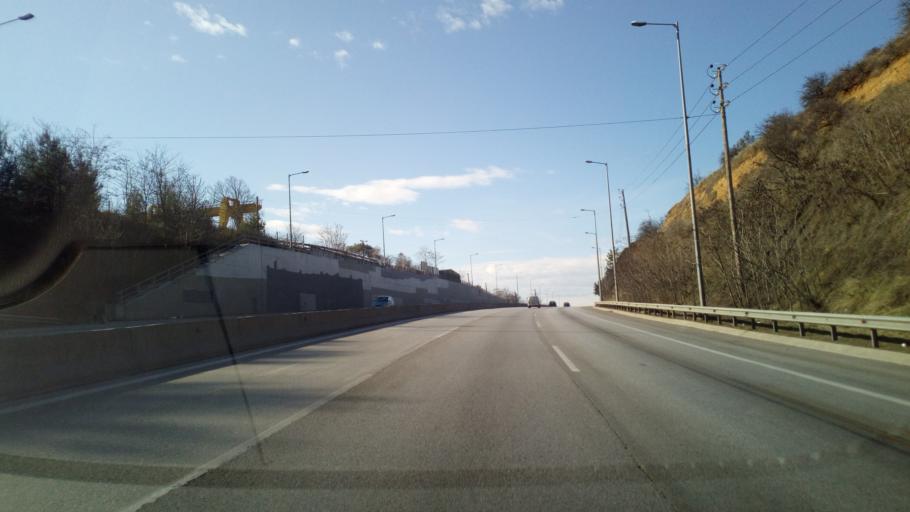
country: GR
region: Central Macedonia
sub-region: Nomos Thessalonikis
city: Liti
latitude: 40.7246
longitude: 22.9794
